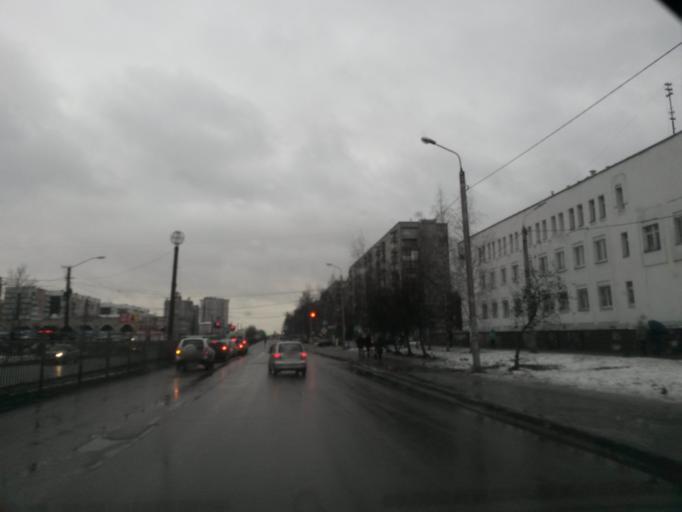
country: RU
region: Jaroslavl
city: Yaroslavl
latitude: 57.6510
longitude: 39.9479
